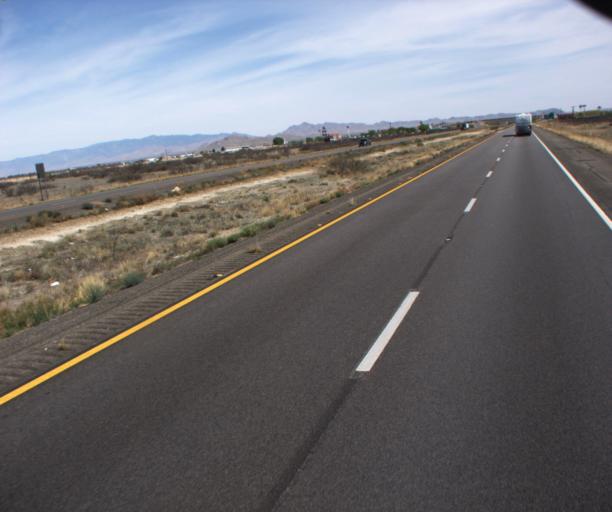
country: US
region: Arizona
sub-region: Cochise County
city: Willcox
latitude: 32.2580
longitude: -109.8502
